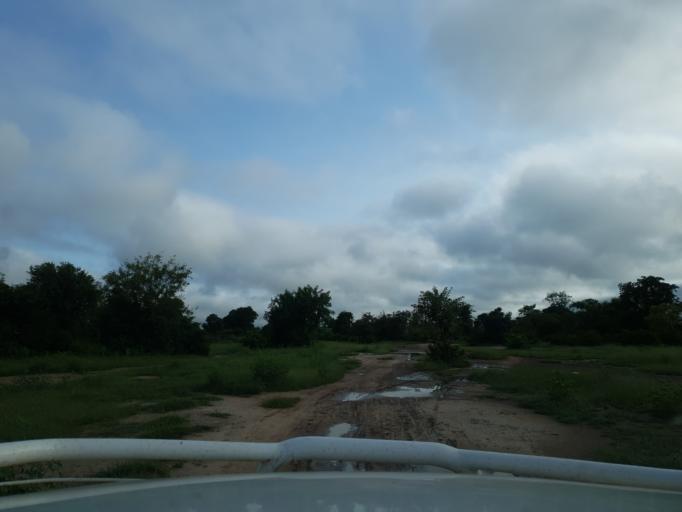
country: ML
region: Segou
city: Baroueli
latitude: 13.3942
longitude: -7.0057
